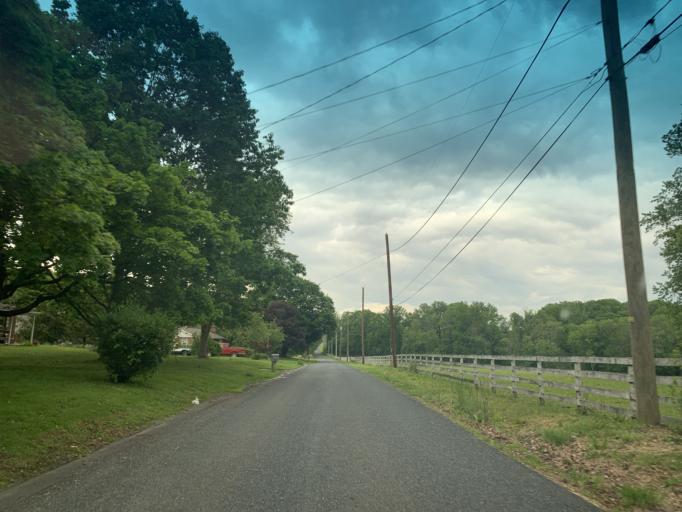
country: US
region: Maryland
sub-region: Harford County
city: Aberdeen
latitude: 39.6550
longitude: -76.2155
